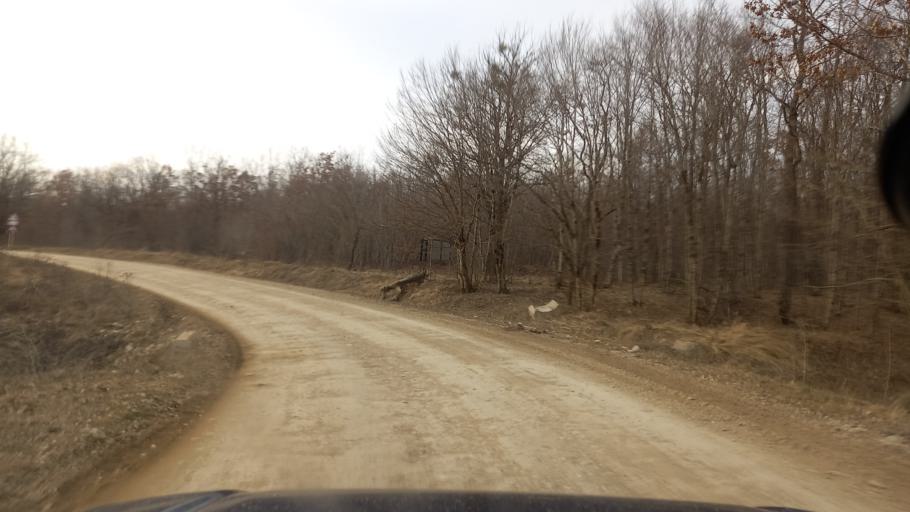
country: RU
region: Adygeya
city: Kamennomostskiy
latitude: 44.1449
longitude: 40.2580
